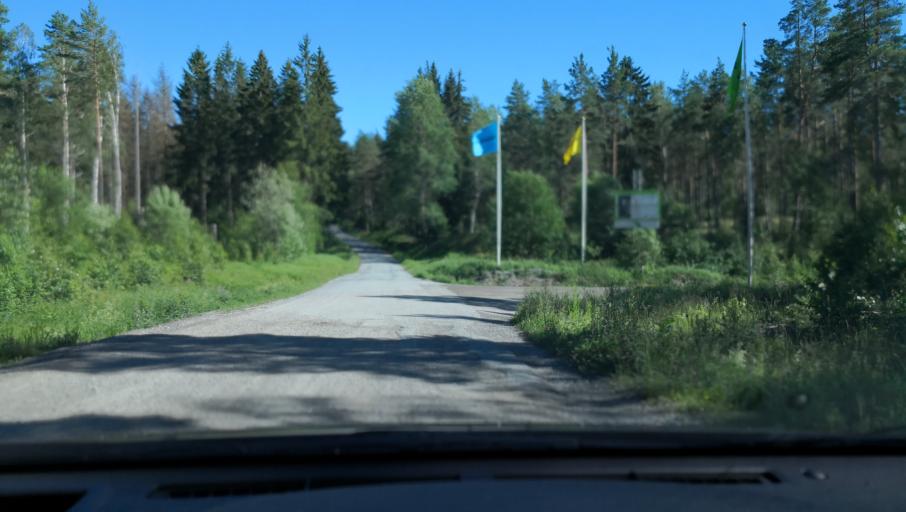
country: SE
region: Soedermanland
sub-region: Eskilstuna Kommun
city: Eskilstuna
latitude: 59.3474
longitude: 16.5509
